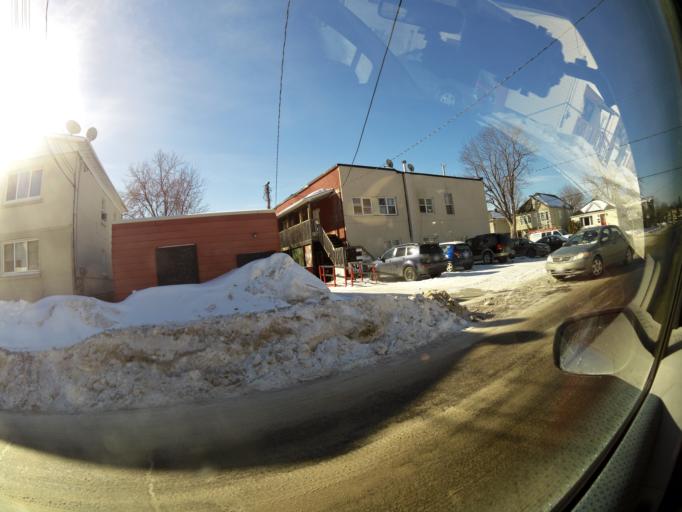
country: CA
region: Ontario
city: Ottawa
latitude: 45.4388
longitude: -75.6738
